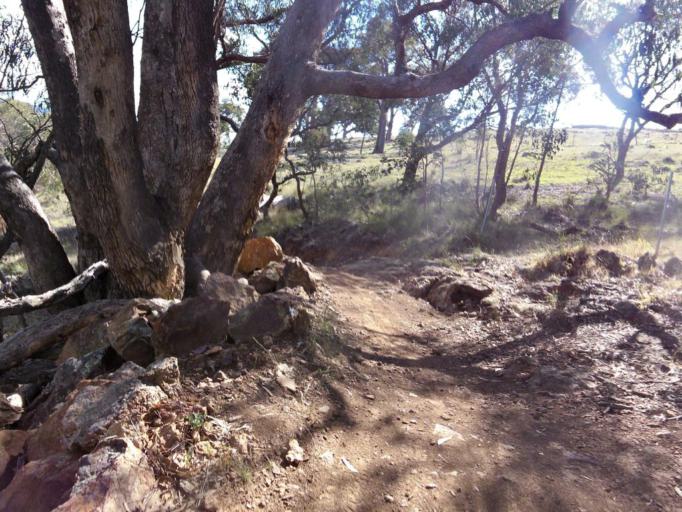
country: AU
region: Australian Capital Territory
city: Belconnen
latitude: -35.1557
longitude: 149.0821
